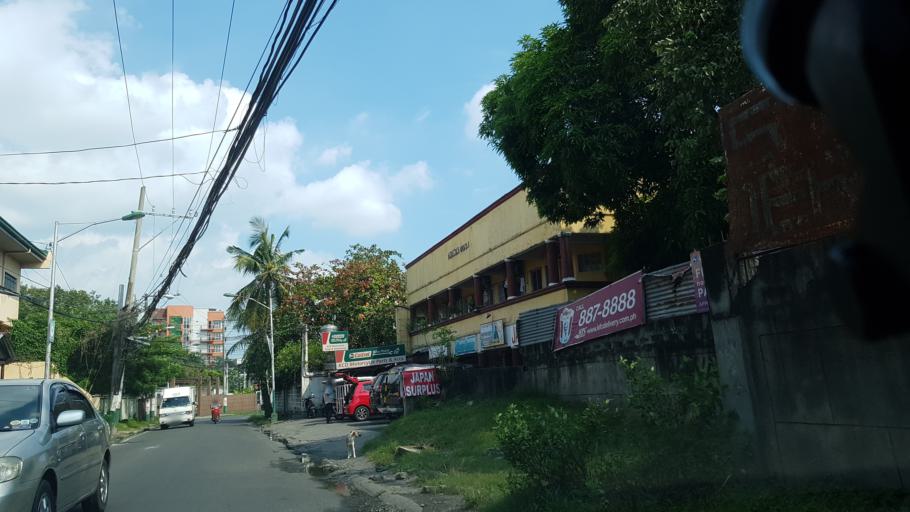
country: PH
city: Sambayanihan People's Village
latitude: 14.4761
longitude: 121.0259
